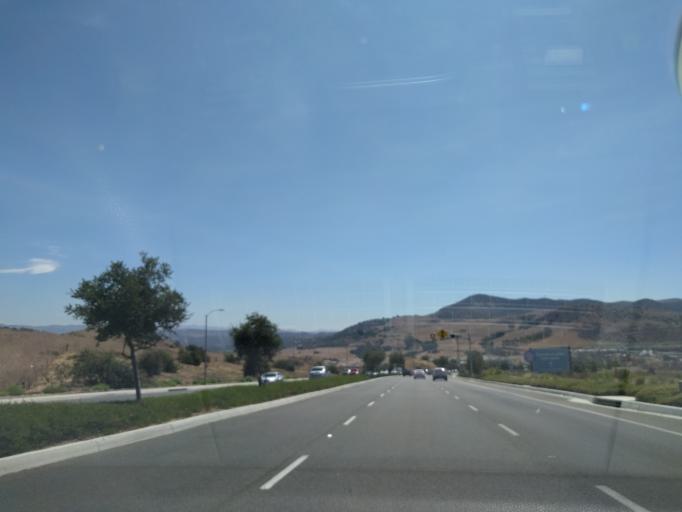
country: US
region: California
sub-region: Orange County
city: Ladera Ranch
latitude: 33.5319
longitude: -117.6214
